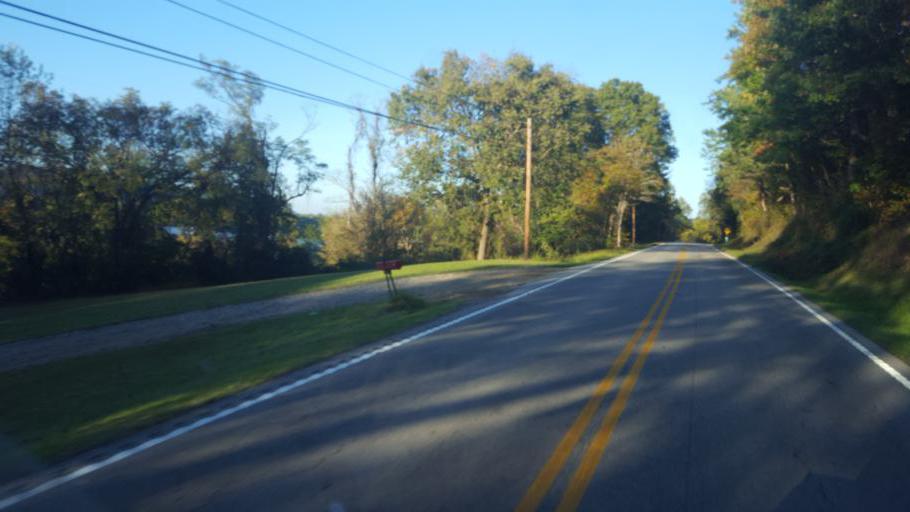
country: US
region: Ohio
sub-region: Scioto County
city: Portsmouth
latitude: 38.6871
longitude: -83.0586
